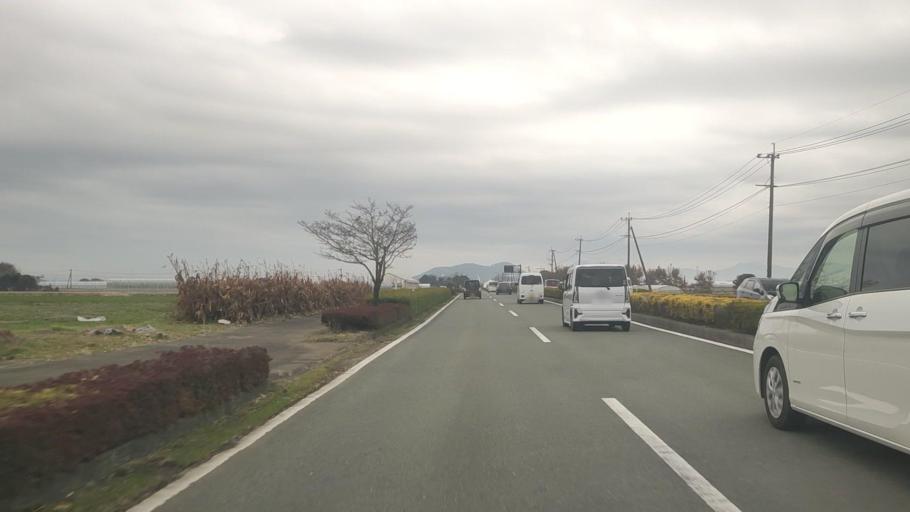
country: JP
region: Kumamoto
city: Ozu
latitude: 32.8458
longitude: 130.8296
